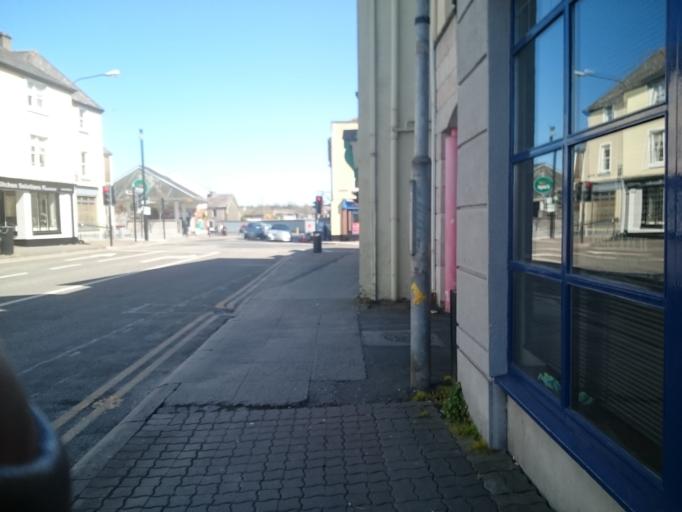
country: IE
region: Leinster
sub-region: Kilkenny
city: Kilkenny
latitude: 52.6557
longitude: -7.2566
